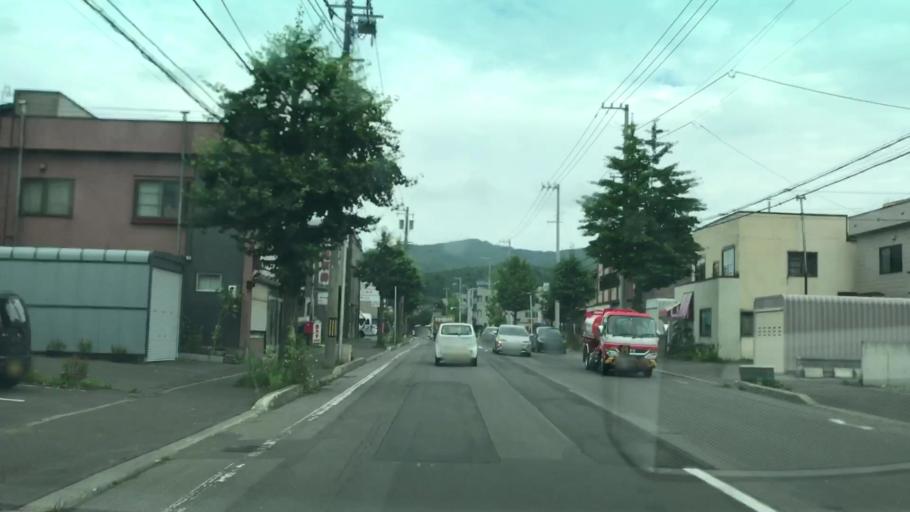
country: JP
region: Hokkaido
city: Otaru
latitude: 43.2045
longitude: 140.9847
